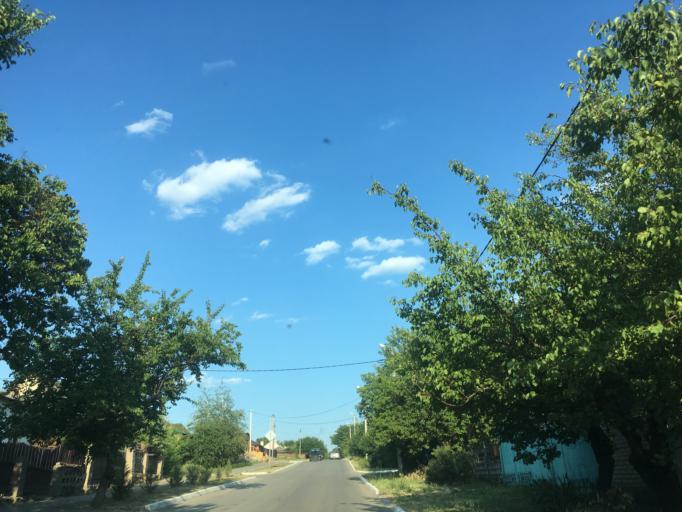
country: RU
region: Rostov
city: Masalovka
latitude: 48.4005
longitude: 40.2780
